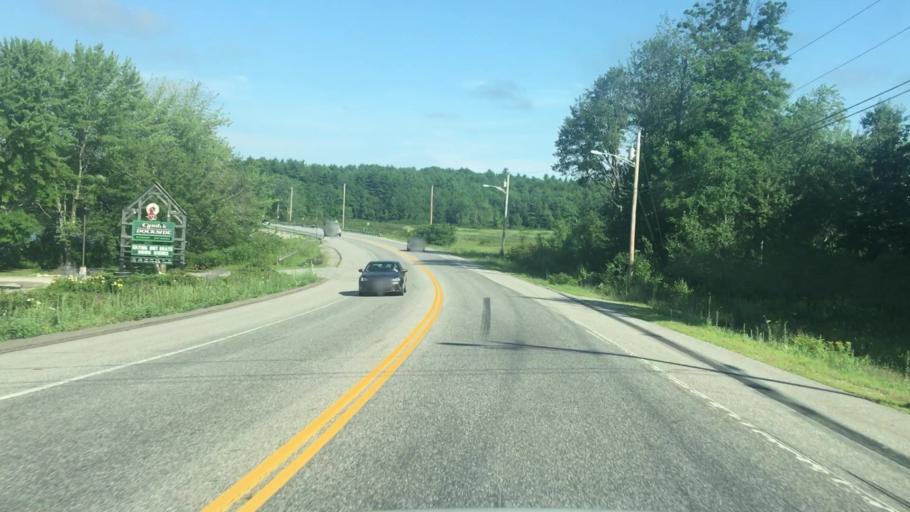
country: US
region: Maine
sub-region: Androscoggin County
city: Poland
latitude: 44.0365
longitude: -70.3703
